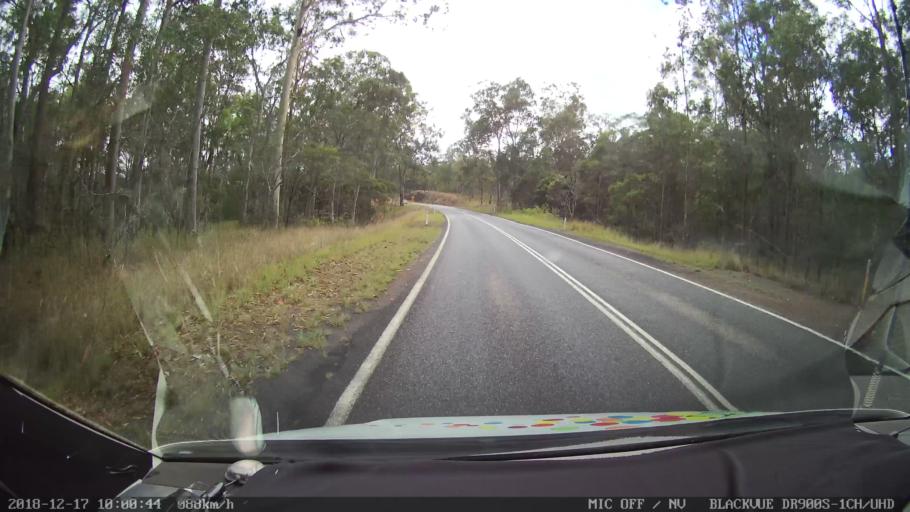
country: AU
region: New South Wales
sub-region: Tenterfield Municipality
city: Carrolls Creek
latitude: -28.9093
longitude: 152.4300
